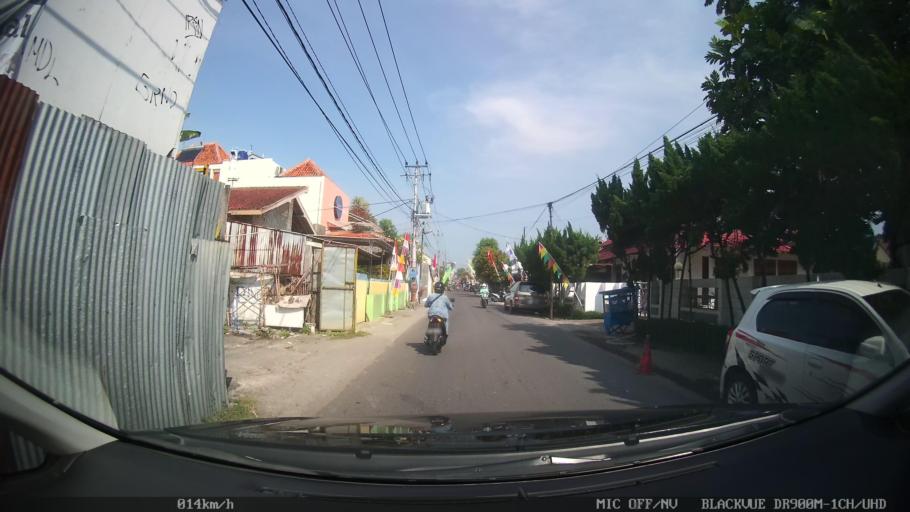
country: ID
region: Daerah Istimewa Yogyakarta
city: Yogyakarta
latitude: -7.7915
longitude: 110.3600
